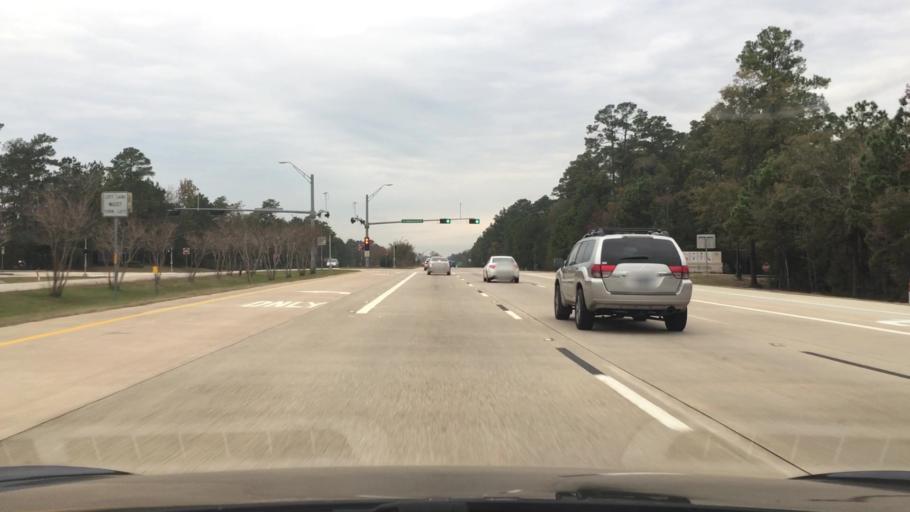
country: US
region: Texas
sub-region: Montgomery County
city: Shenandoah
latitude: 30.2071
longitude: -95.4672
